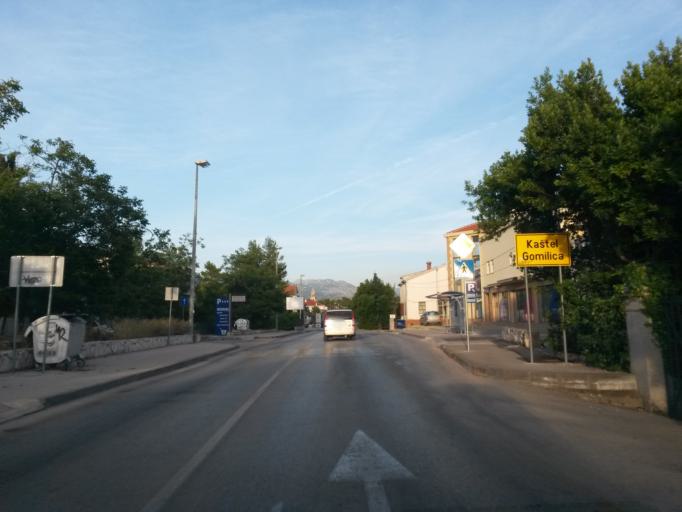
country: HR
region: Splitsko-Dalmatinska
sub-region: Grad Split
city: Split
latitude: 43.5496
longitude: 16.3903
